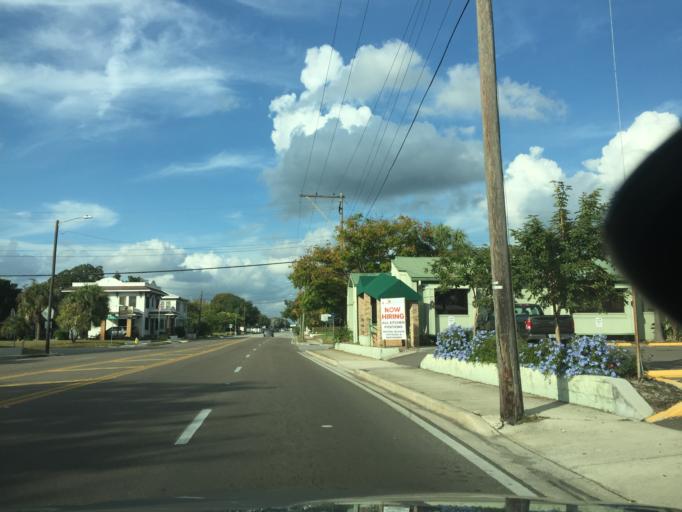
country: US
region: Florida
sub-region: Hillsborough County
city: Tampa
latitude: 27.9454
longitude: -82.4932
